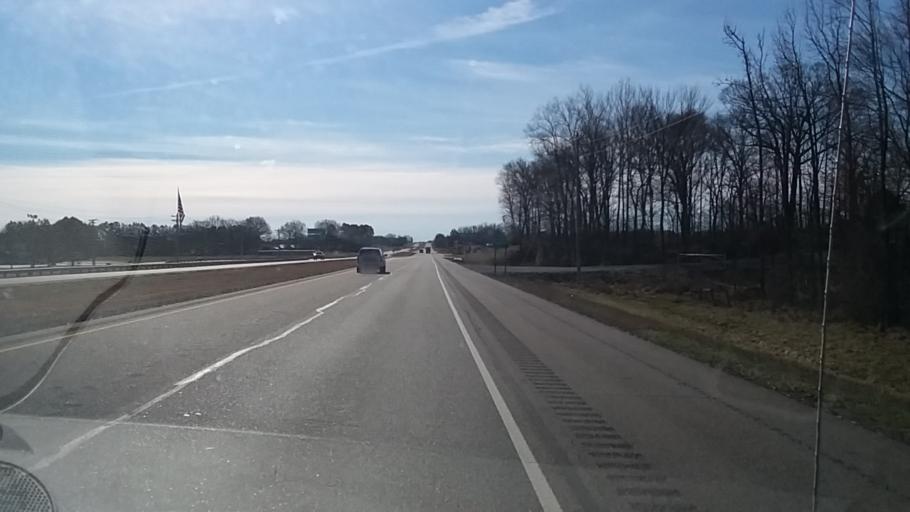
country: US
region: Tennessee
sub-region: Lauderdale County
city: Halls
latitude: 35.9037
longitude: -89.2537
